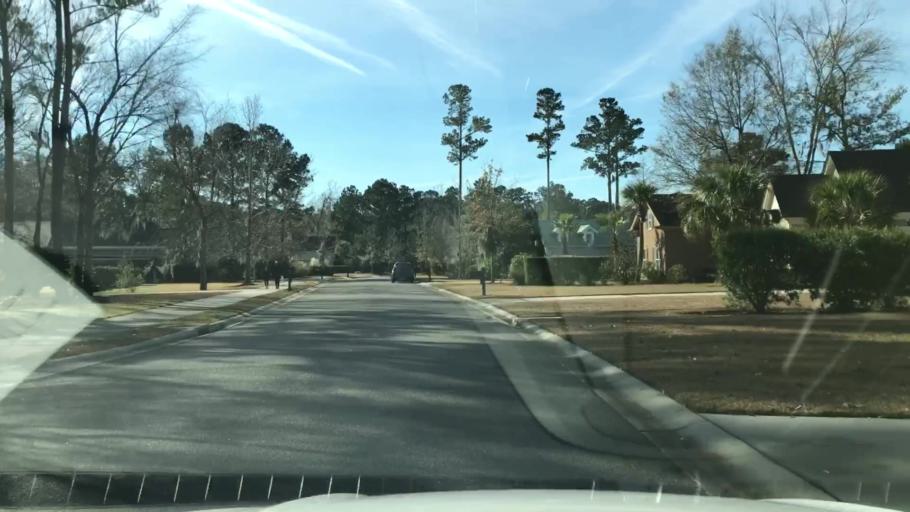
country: US
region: South Carolina
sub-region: Beaufort County
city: Bluffton
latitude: 32.2411
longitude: -80.9144
